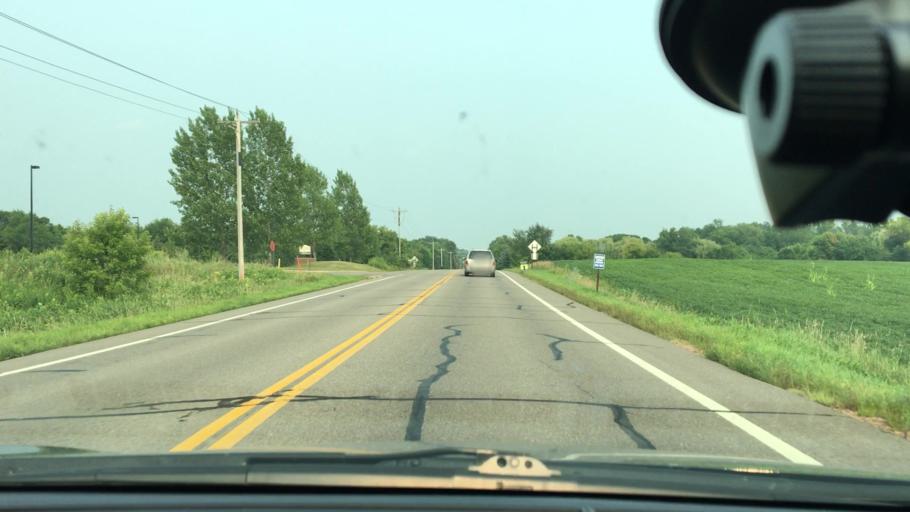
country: US
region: Minnesota
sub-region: Hennepin County
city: Champlin
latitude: 45.1881
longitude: -93.4602
